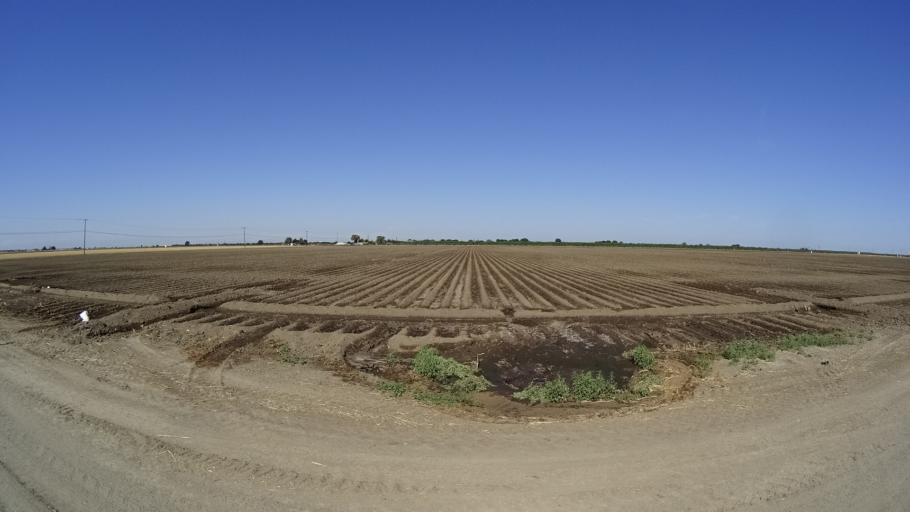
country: US
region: California
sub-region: Kings County
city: Home Garden
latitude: 36.2562
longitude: -119.5474
